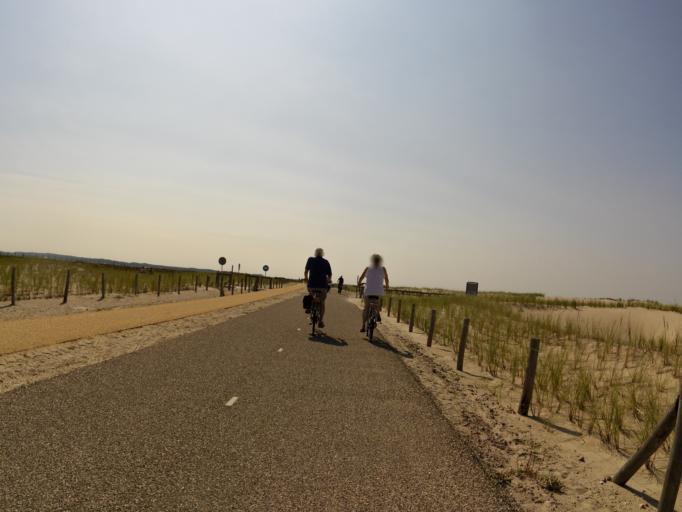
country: NL
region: North Holland
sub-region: Gemeente Schagen
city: Harenkarspel
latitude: 52.7673
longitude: 4.6541
